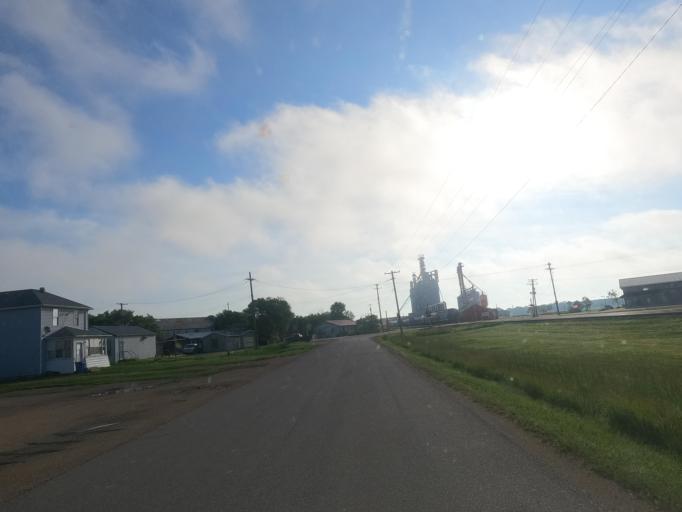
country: CA
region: Manitoba
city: Headingley
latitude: 49.7695
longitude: -97.6198
